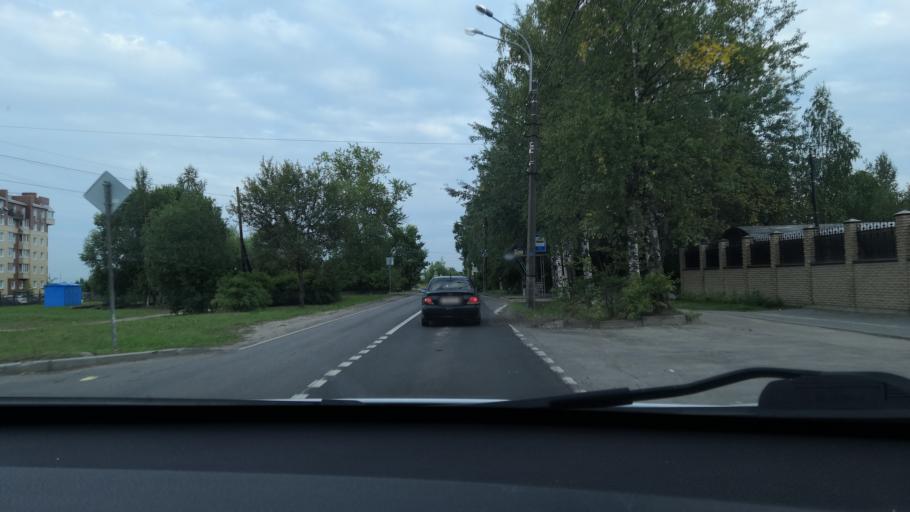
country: RU
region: St.-Petersburg
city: Pushkin
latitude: 59.6968
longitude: 30.4118
